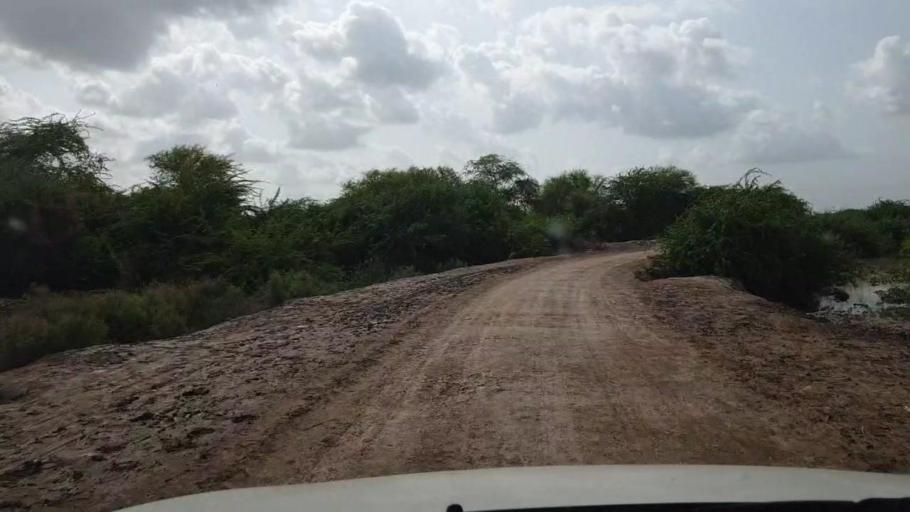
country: PK
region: Sindh
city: Kario
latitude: 24.7158
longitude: 68.6384
